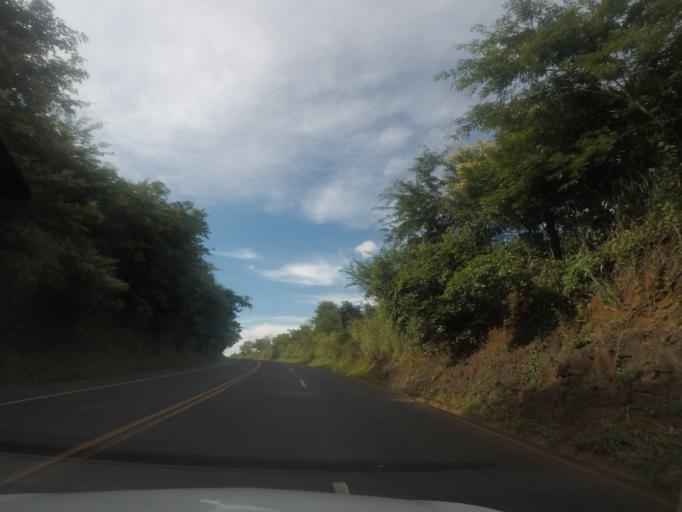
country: BR
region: Minas Gerais
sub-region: Monte Alegre De Minas
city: Monte Alegre de Minas
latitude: -18.9451
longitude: -49.0254
